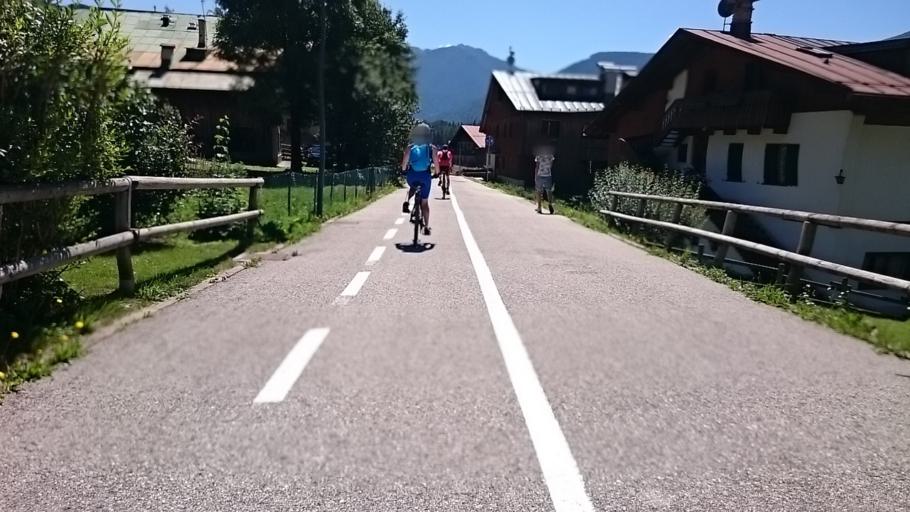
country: IT
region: Veneto
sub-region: Provincia di Belluno
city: San Vito
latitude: 46.4547
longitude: 12.2085
